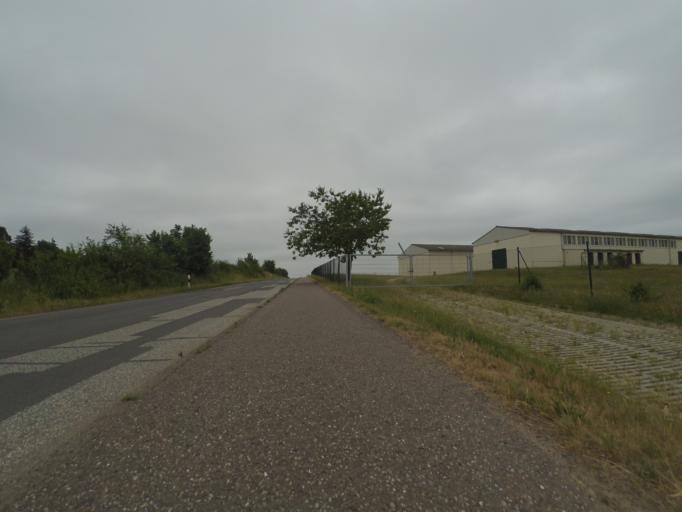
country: DE
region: Mecklenburg-Vorpommern
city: Sternberg
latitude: 53.6856
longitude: 11.8211
